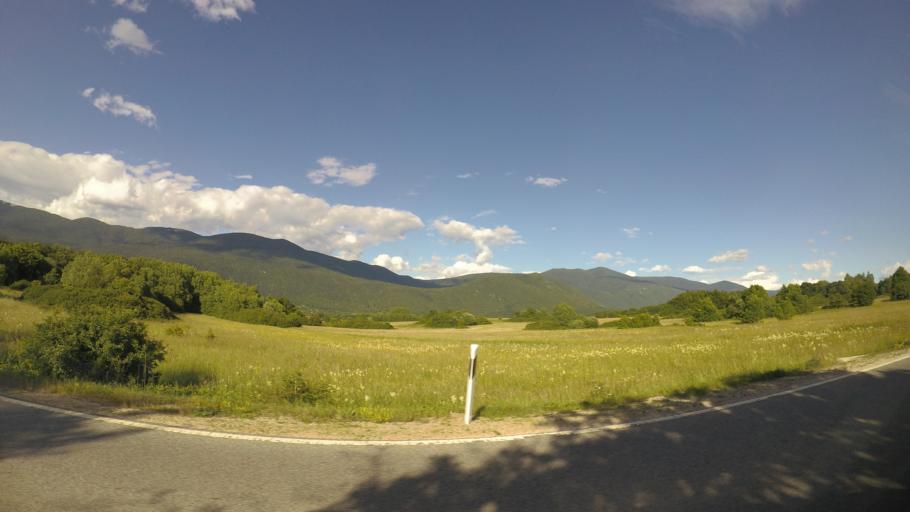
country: BA
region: Federation of Bosnia and Herzegovina
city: Izacic
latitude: 44.7246
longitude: 15.7353
